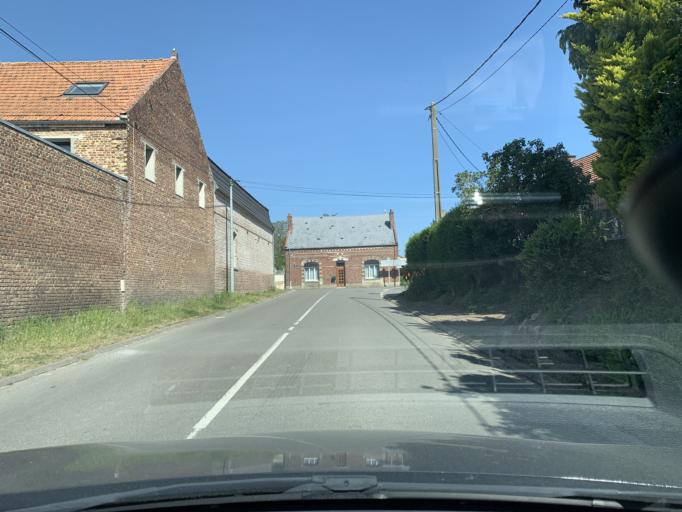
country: FR
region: Nord-Pas-de-Calais
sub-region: Departement du Nord
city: Fontaine-Notre-Dame
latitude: 50.1490
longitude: 3.1663
